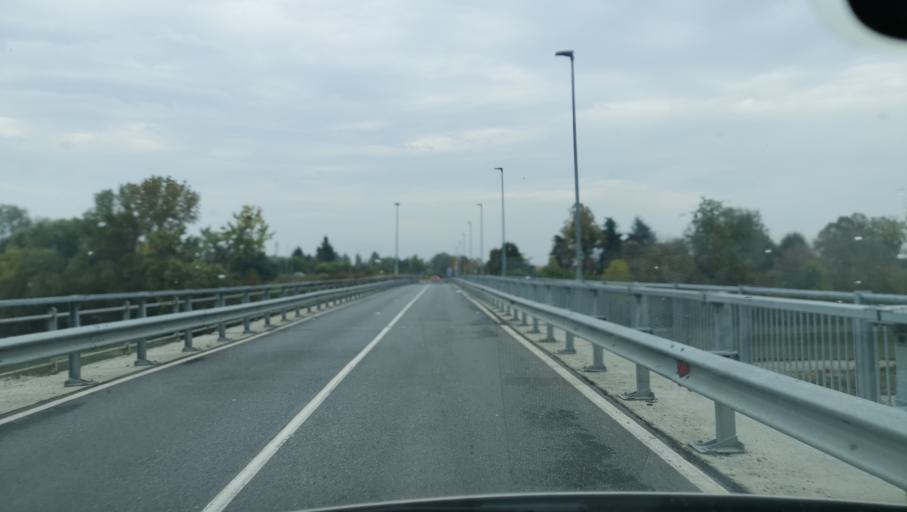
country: IT
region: Piedmont
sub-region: Provincia di Torino
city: Settimo Torinese
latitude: 45.1296
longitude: 7.7847
